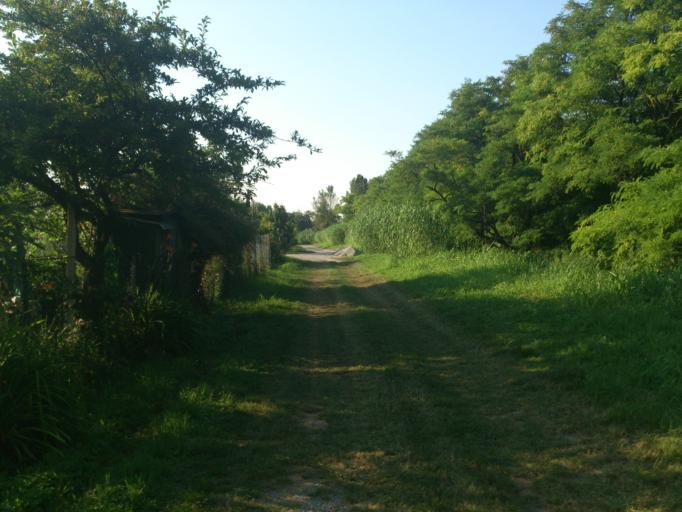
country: IT
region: Lombardy
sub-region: Citta metropolitana di Milano
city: San Donato Milanese
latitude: 45.4235
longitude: 9.2786
